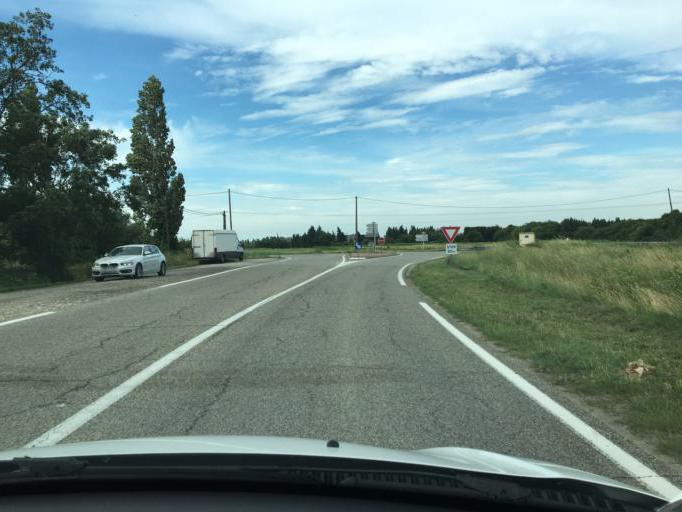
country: FR
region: Provence-Alpes-Cote d'Azur
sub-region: Departement du Vaucluse
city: Bollene
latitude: 44.2918
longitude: 4.7311
